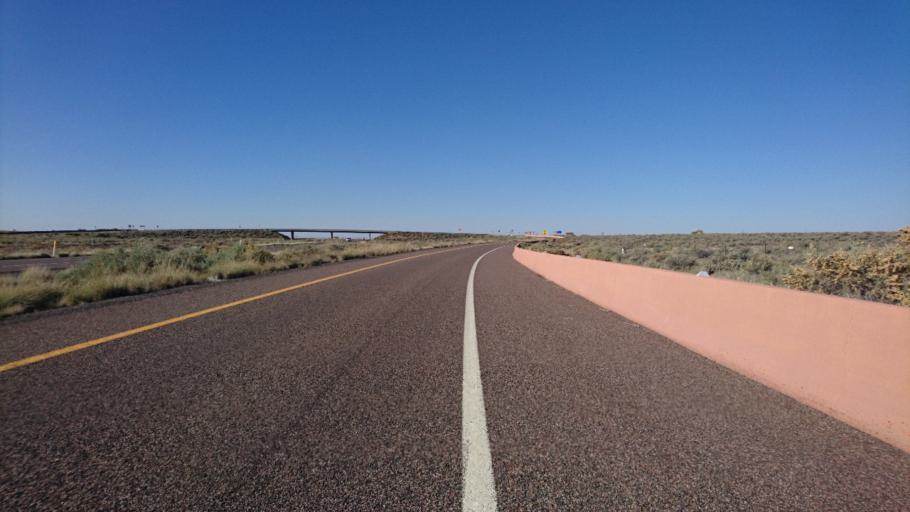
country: US
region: Arizona
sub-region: Navajo County
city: Holbrook
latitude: 35.0623
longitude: -109.7784
